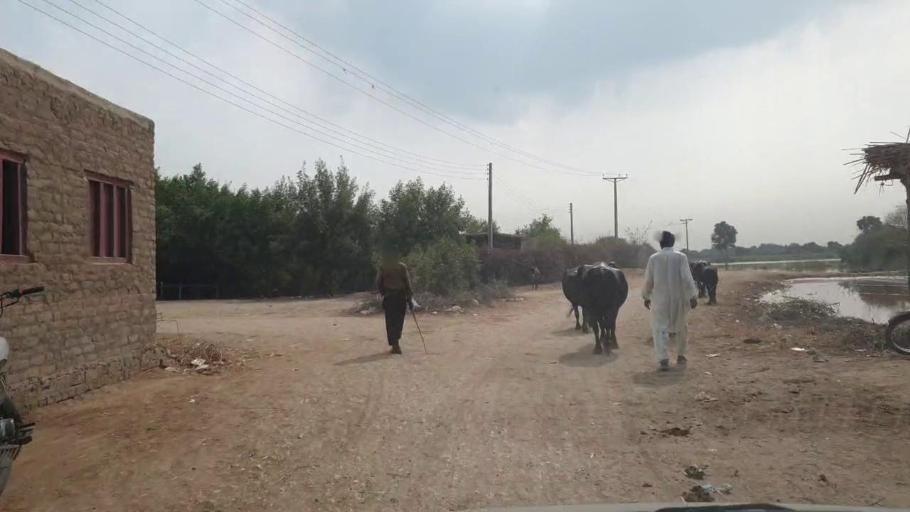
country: PK
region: Sindh
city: Matli
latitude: 24.9566
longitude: 68.7116
